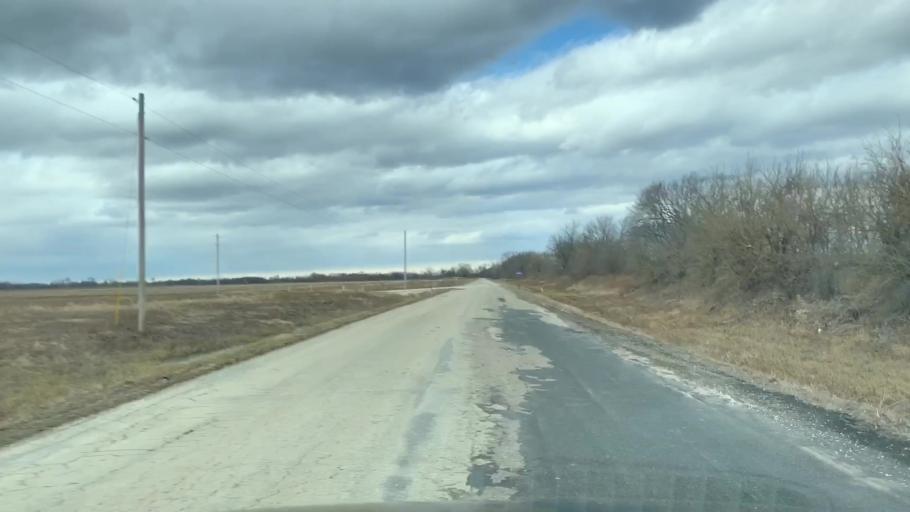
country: US
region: Kansas
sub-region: Allen County
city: Humboldt
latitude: 37.7902
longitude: -95.4706
